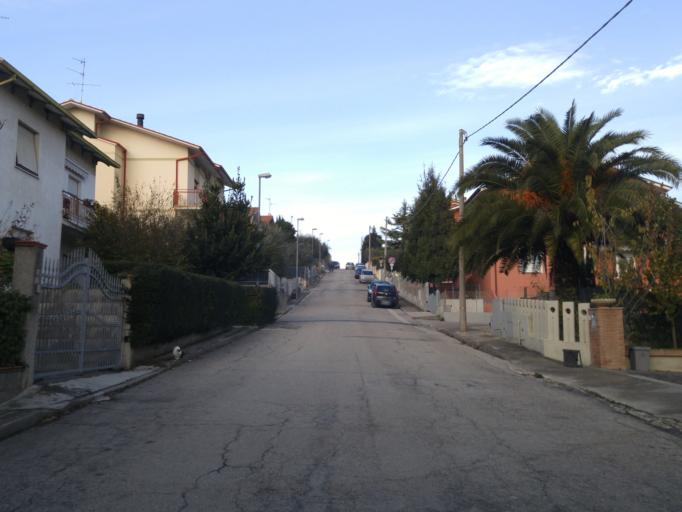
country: IT
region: The Marches
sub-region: Provincia di Pesaro e Urbino
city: Lucrezia
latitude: 43.7699
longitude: 12.9301
